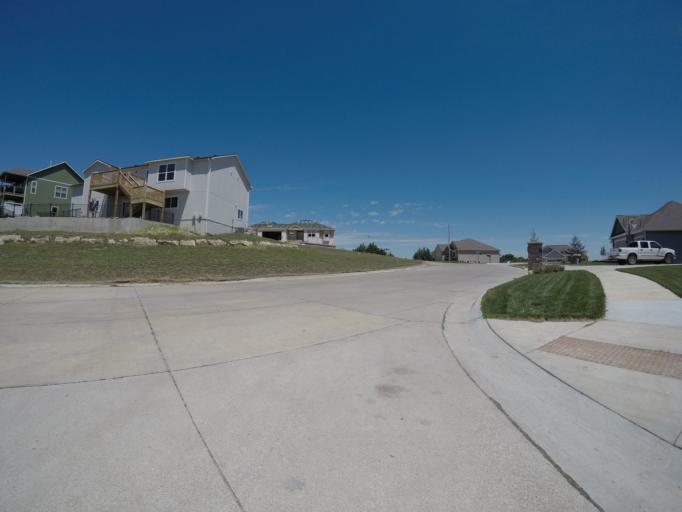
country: US
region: Kansas
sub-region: Riley County
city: Manhattan
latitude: 39.1736
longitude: -96.6302
